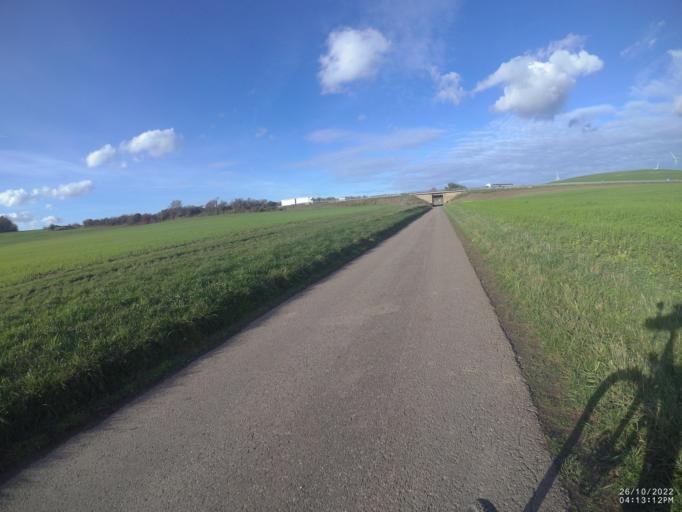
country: DE
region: Baden-Wuerttemberg
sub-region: Regierungsbezirk Stuttgart
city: Hohenstadt
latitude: 48.5296
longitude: 9.6785
